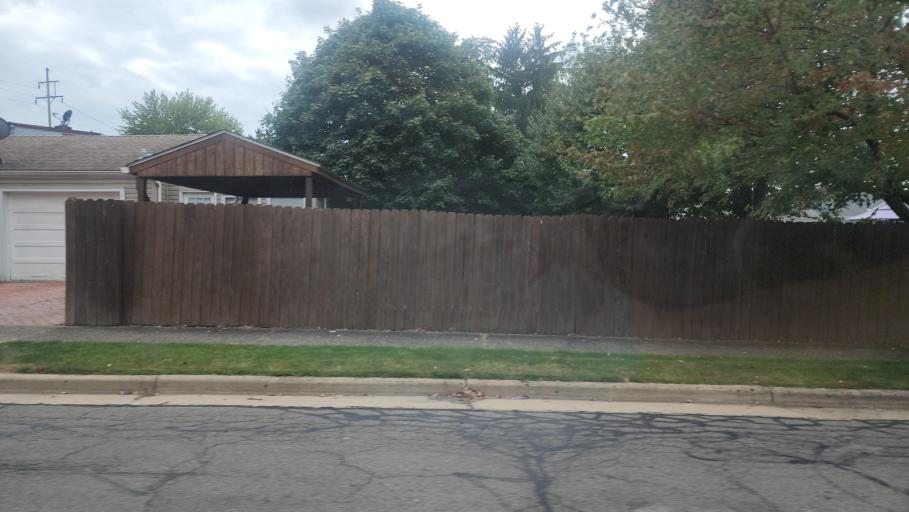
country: US
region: Ohio
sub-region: Mahoning County
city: Struthers
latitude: 41.0552
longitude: -80.6260
